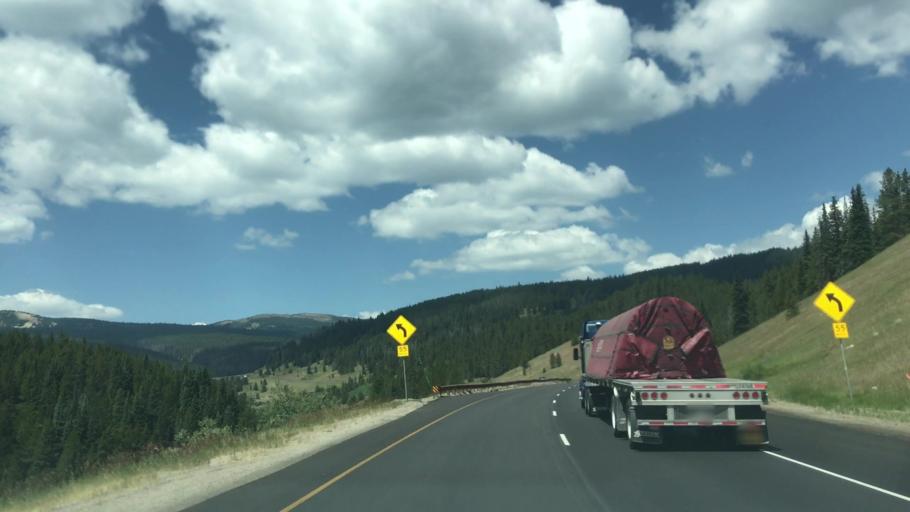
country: US
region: Colorado
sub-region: Summit County
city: Frisco
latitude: 39.5046
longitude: -106.1789
